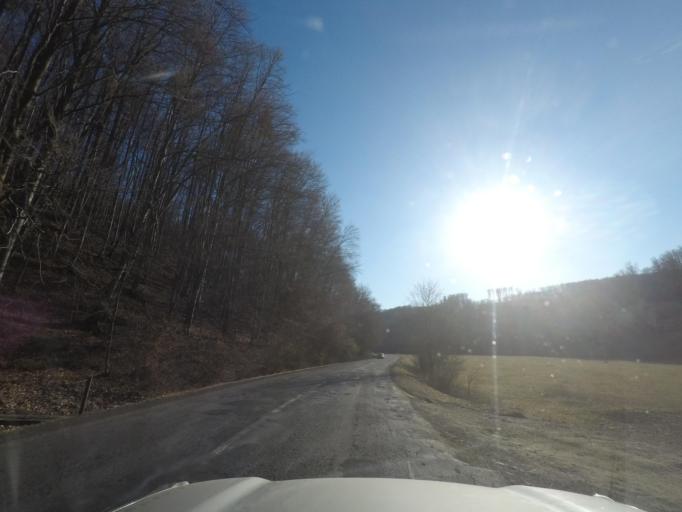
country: SK
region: Presovsky
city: Medzilaborce
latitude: 49.2736
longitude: 21.8038
